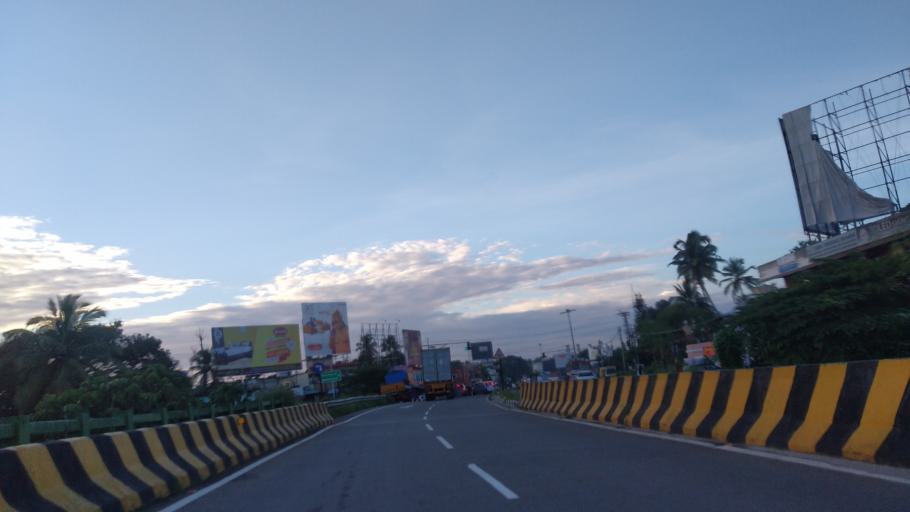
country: IN
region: Kerala
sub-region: Ernakulam
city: Elur
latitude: 10.0665
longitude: 76.3232
